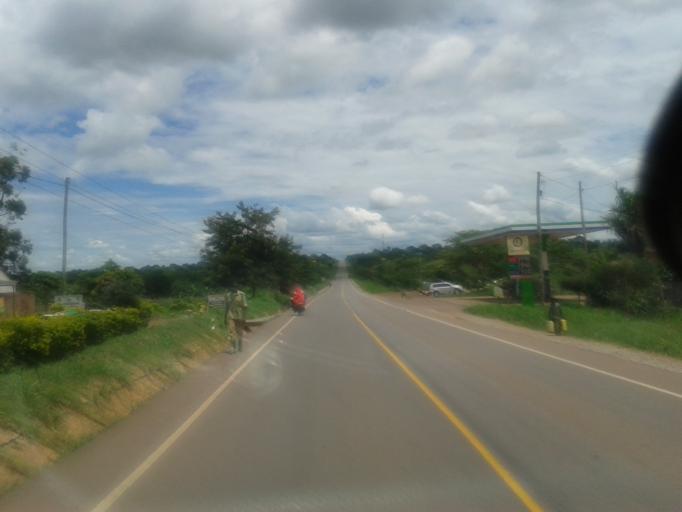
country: UG
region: Western Region
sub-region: Kiryandongo District
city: Kiryandongo
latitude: 1.8734
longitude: 32.0579
